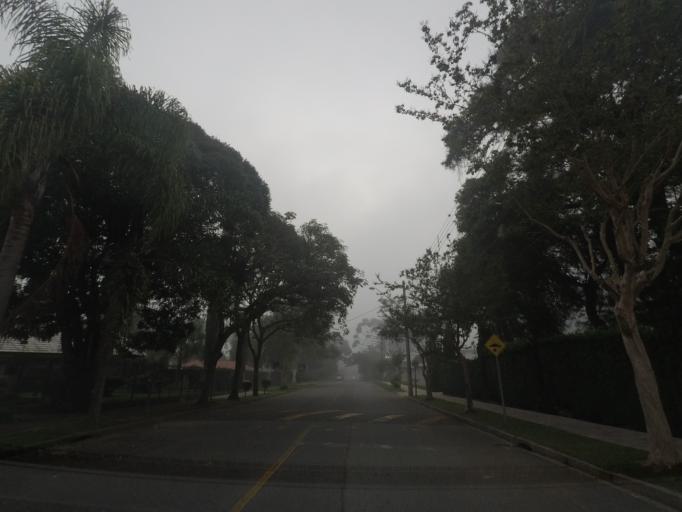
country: BR
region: Parana
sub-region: Curitiba
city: Curitiba
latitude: -25.4441
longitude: -49.2953
